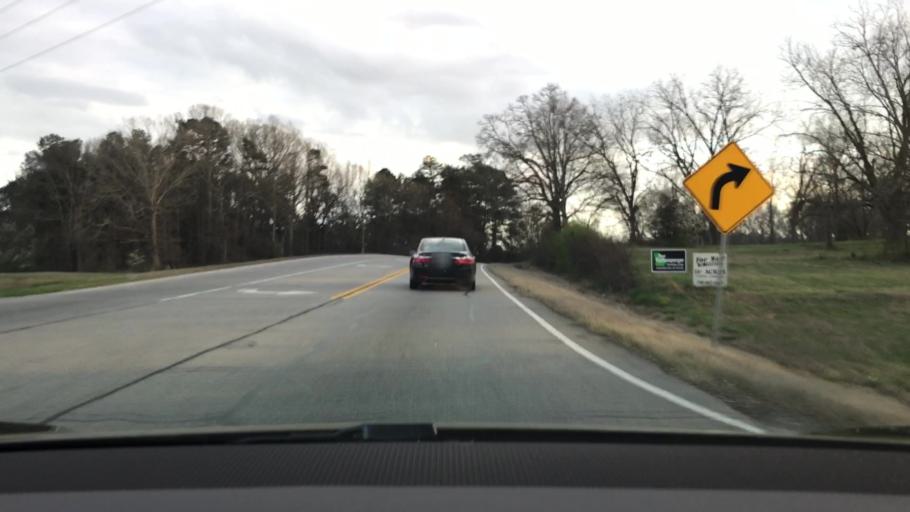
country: US
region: Georgia
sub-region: Barrow County
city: Russell
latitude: 33.9199
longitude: -83.7158
